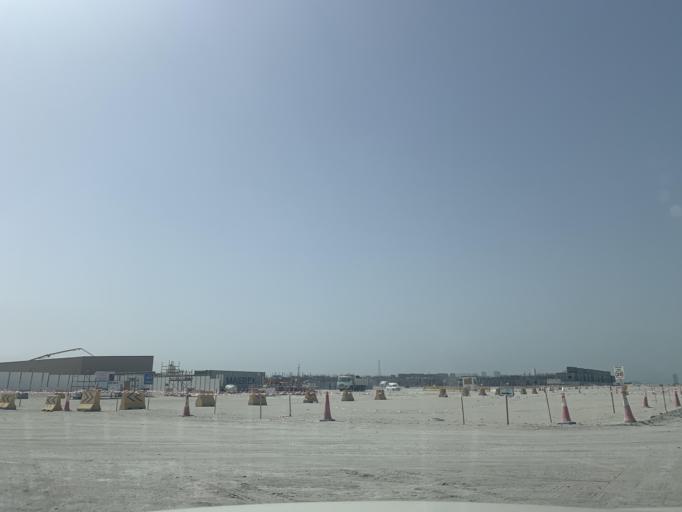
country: BH
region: Northern
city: Sitrah
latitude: 26.1626
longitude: 50.6362
